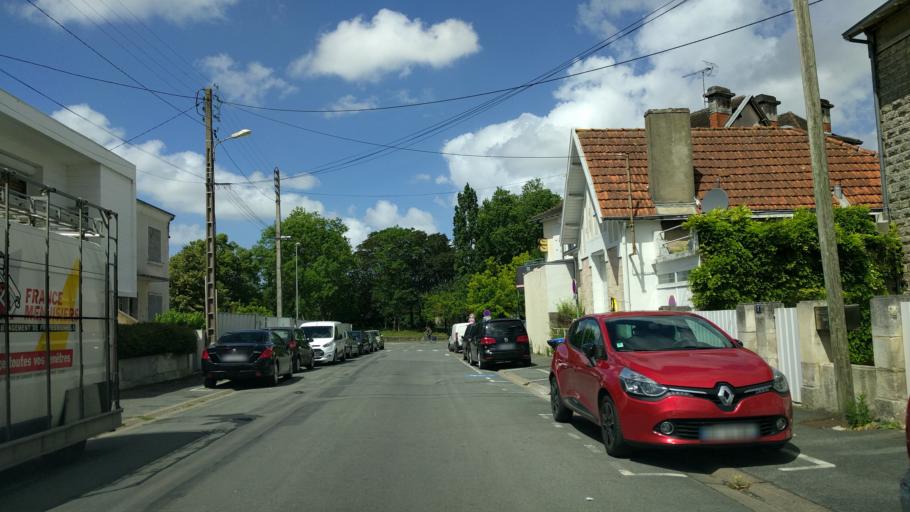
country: FR
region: Poitou-Charentes
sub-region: Departement de la Charente-Maritime
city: La Rochelle
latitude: 46.1686
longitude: -1.1489
